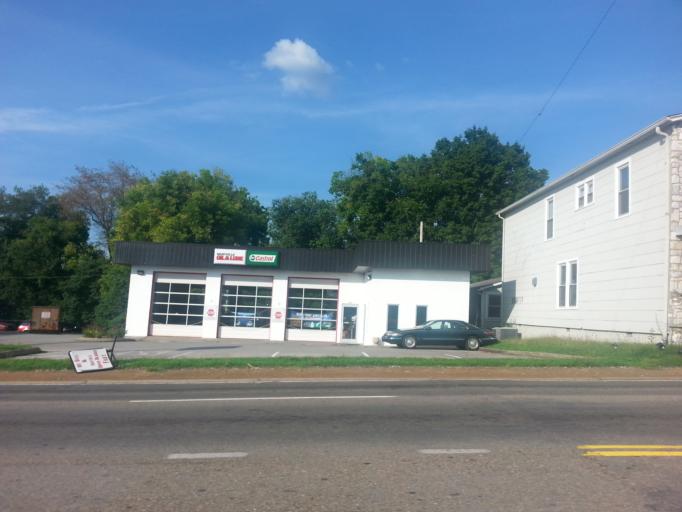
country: US
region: Tennessee
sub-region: Blount County
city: Maryville
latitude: 35.7597
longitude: -83.9666
